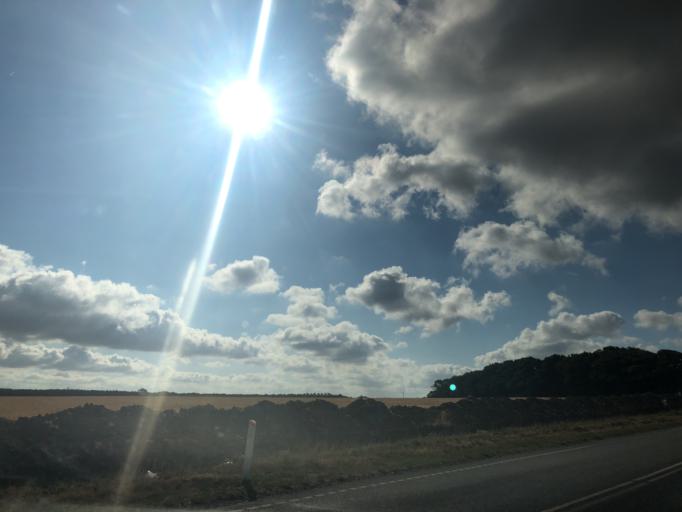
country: DK
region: Central Jutland
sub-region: Holstebro Kommune
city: Vinderup
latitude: 56.6275
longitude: 8.8470
